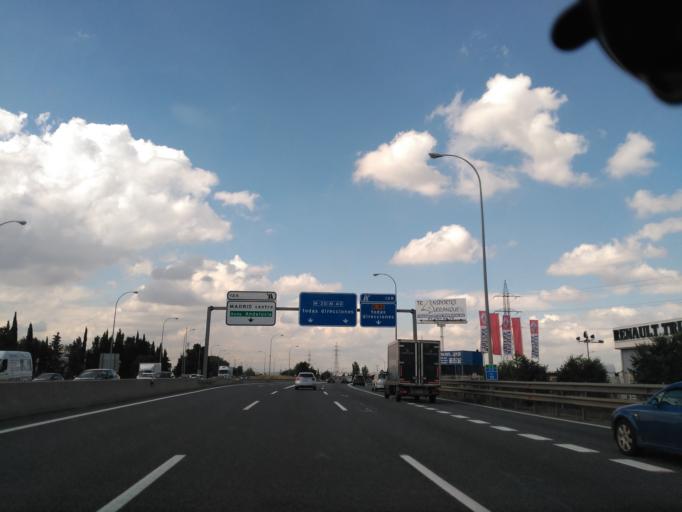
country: ES
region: Madrid
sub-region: Provincia de Madrid
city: Villaverde
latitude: 40.3199
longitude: -3.6921
